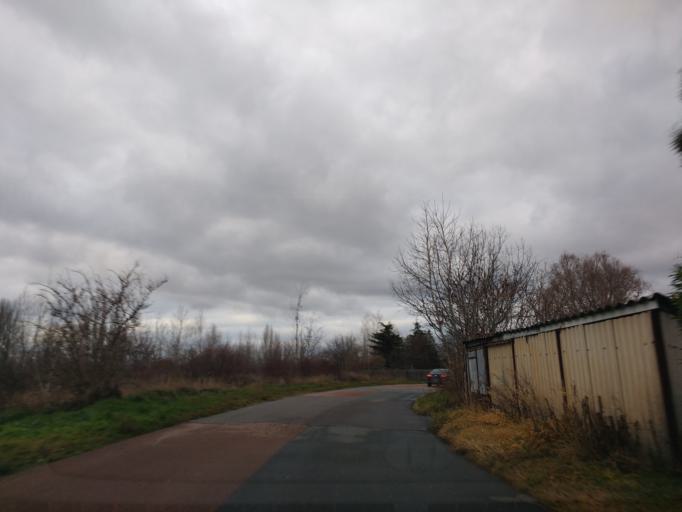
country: DE
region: Saxony-Anhalt
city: Braunsbedra
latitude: 51.2922
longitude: 11.8701
